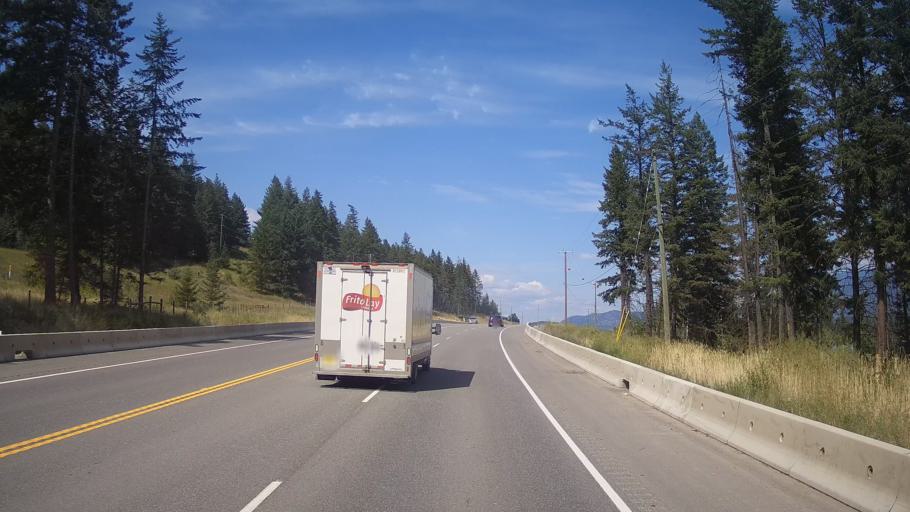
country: CA
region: British Columbia
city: Kamloops
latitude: 51.2746
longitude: -120.1783
